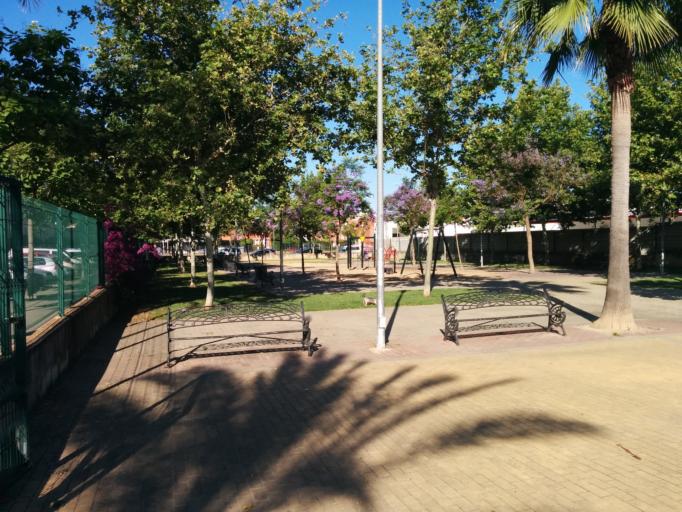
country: ES
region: Andalusia
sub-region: Provincia de Sevilla
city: Sevilla
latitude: 37.4047
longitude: -5.9206
